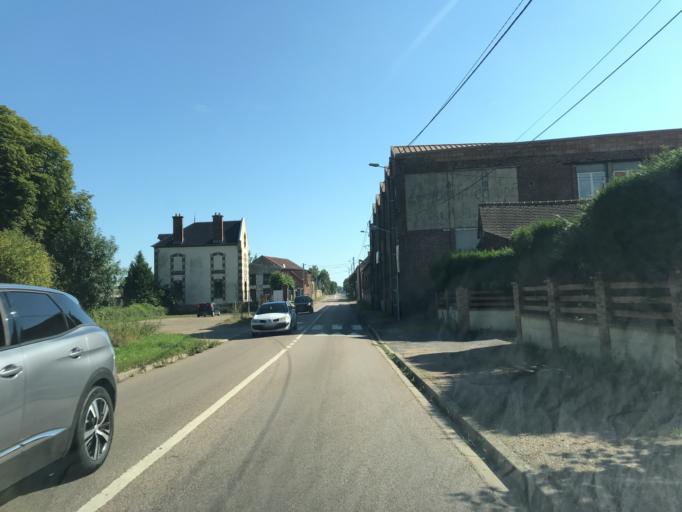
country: FR
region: Ile-de-France
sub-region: Departement du Val-d'Oise
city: Magny-en-Vexin
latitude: 49.1466
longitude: 1.7668
